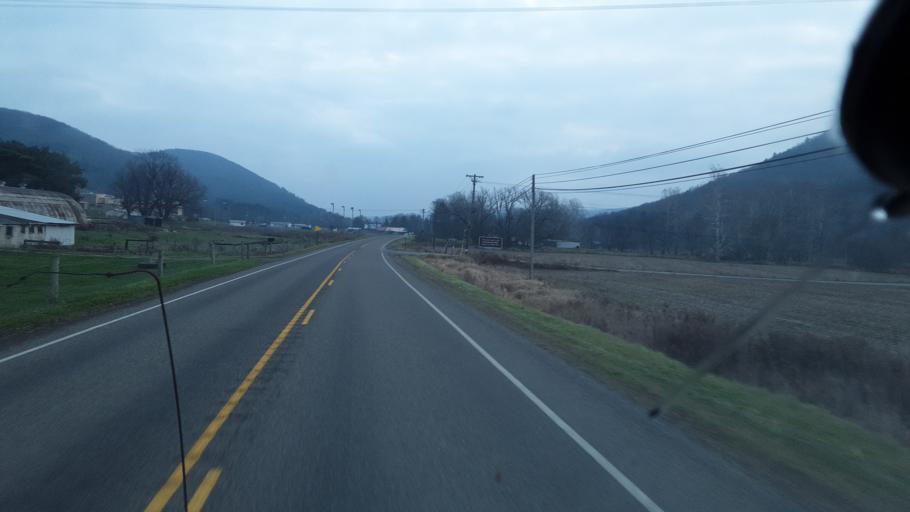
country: US
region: Pennsylvania
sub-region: Tioga County
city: Westfield
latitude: 41.9166
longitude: -77.5725
